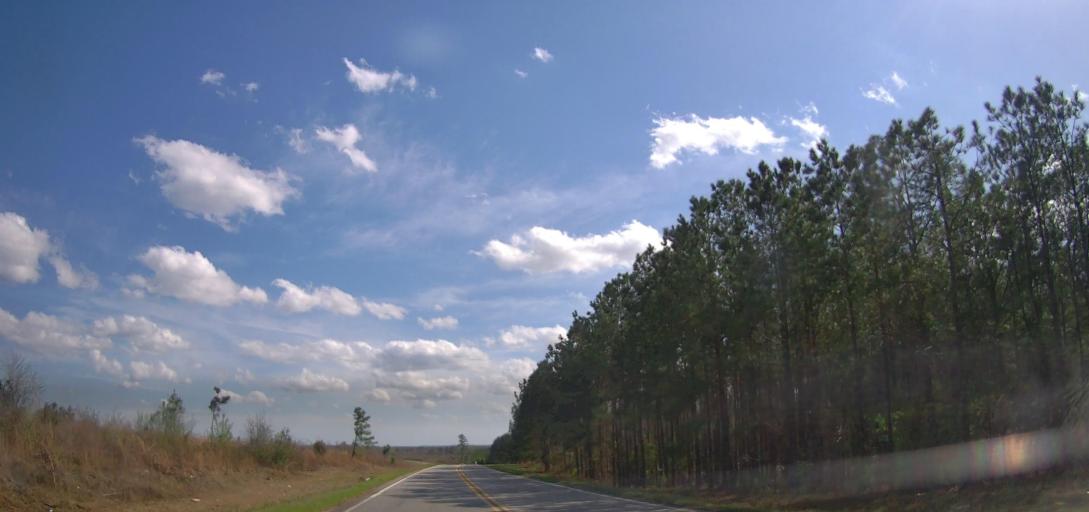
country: US
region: Georgia
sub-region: Wilkinson County
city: Gordon
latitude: 32.9454
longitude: -83.2900
